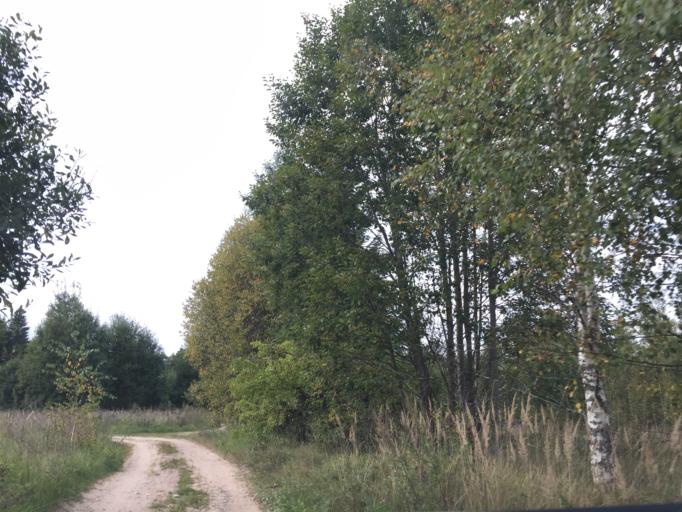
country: LV
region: Baldone
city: Baldone
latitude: 56.7665
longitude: 24.4595
